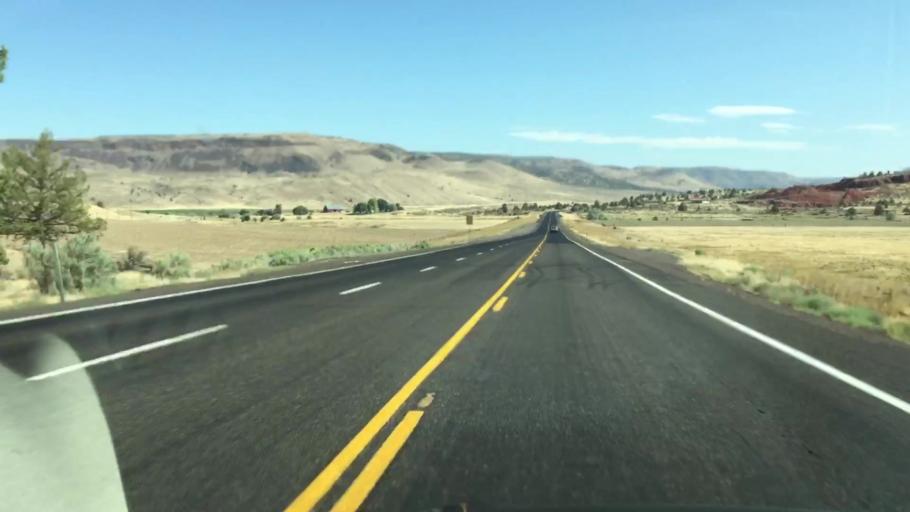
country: US
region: Oregon
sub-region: Jefferson County
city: Madras
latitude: 44.7697
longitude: -120.9705
